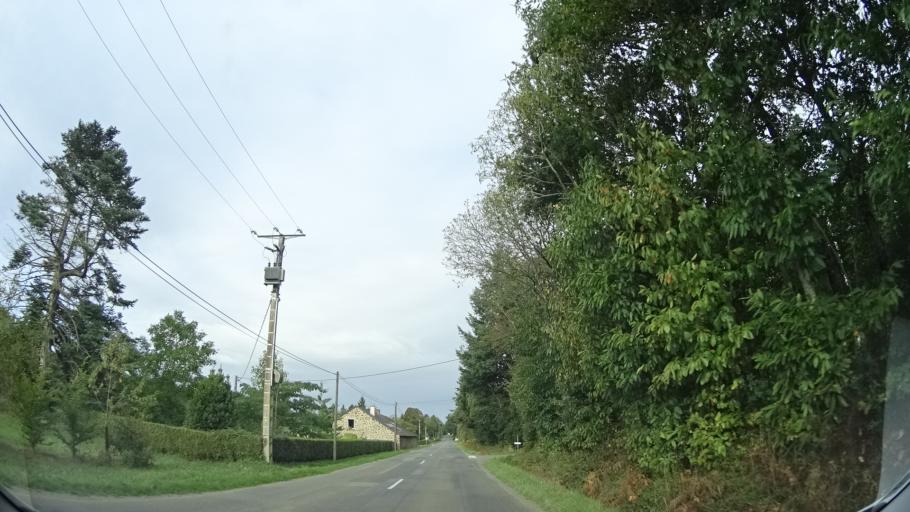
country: FR
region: Brittany
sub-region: Departement d'Ille-et-Vilaine
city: Guipel
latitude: 48.2990
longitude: -1.7414
